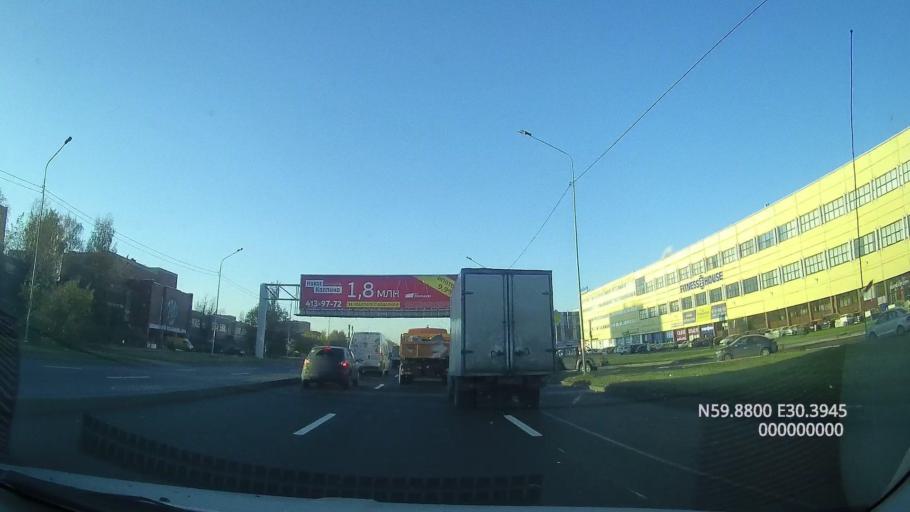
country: RU
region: St.-Petersburg
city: Kupchino
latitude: 59.8801
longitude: 30.3940
